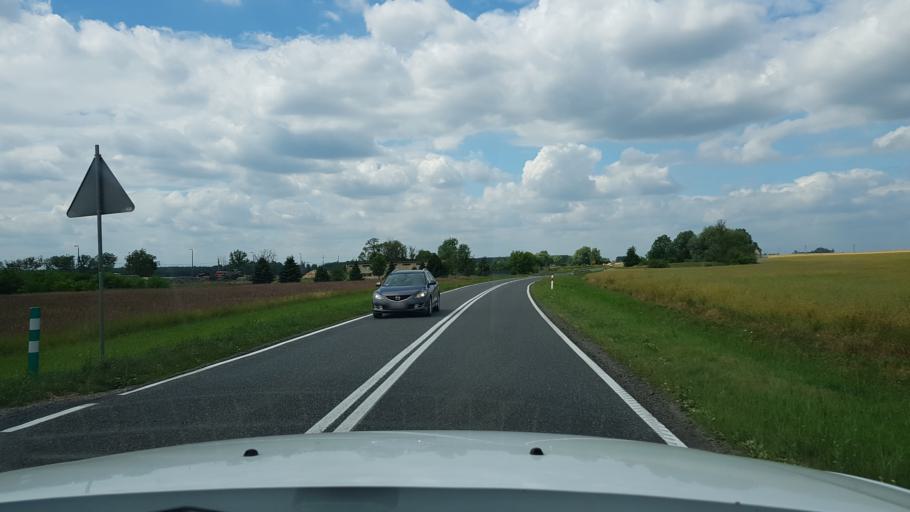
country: PL
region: West Pomeranian Voivodeship
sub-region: Powiat mysliborski
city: Boleszkowice
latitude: 52.7380
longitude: 14.5204
